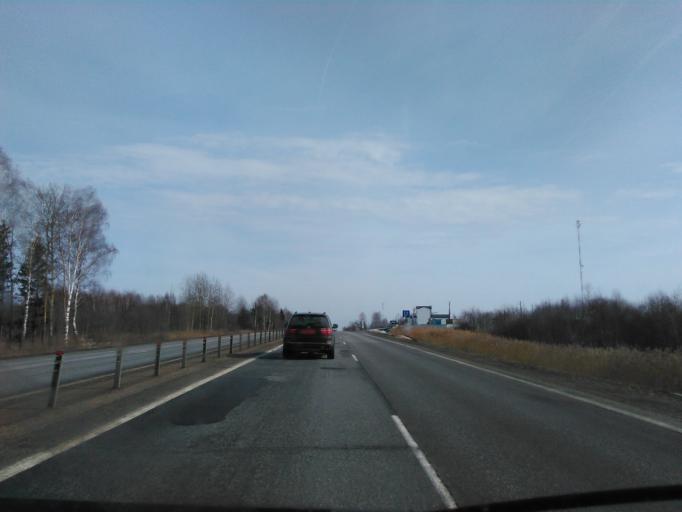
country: BY
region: Vitebsk
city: Dubrowna
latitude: 54.6882
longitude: 30.8681
